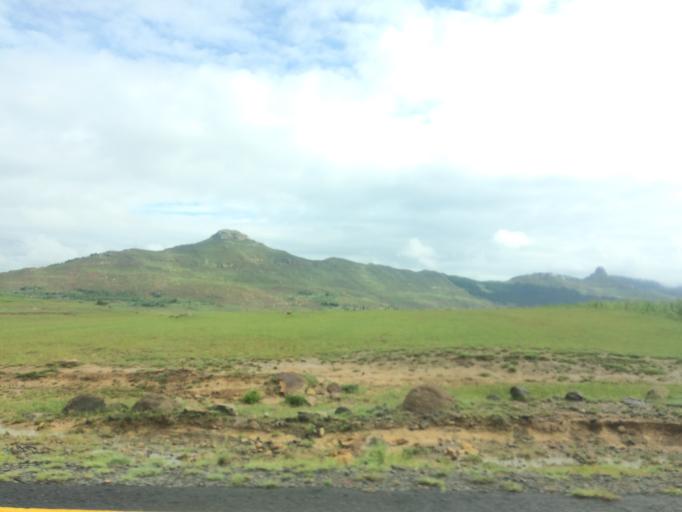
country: LS
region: Mafeteng
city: Mafeteng
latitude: -29.7069
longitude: 27.4688
